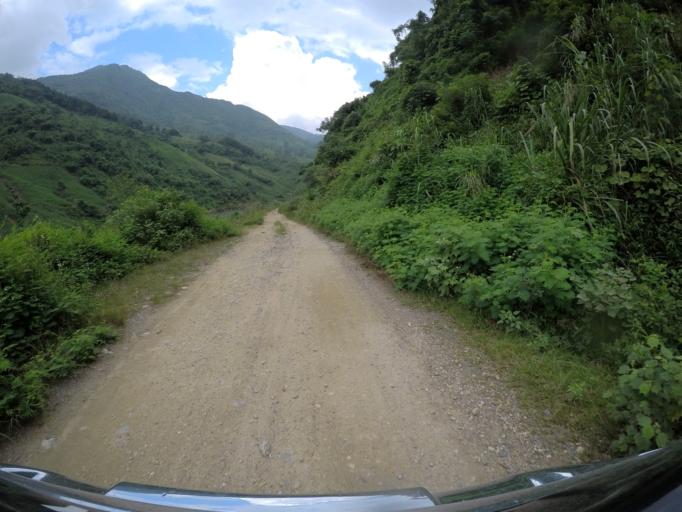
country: VN
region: Yen Bai
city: Son Thinh
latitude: 21.6681
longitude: 104.5186
